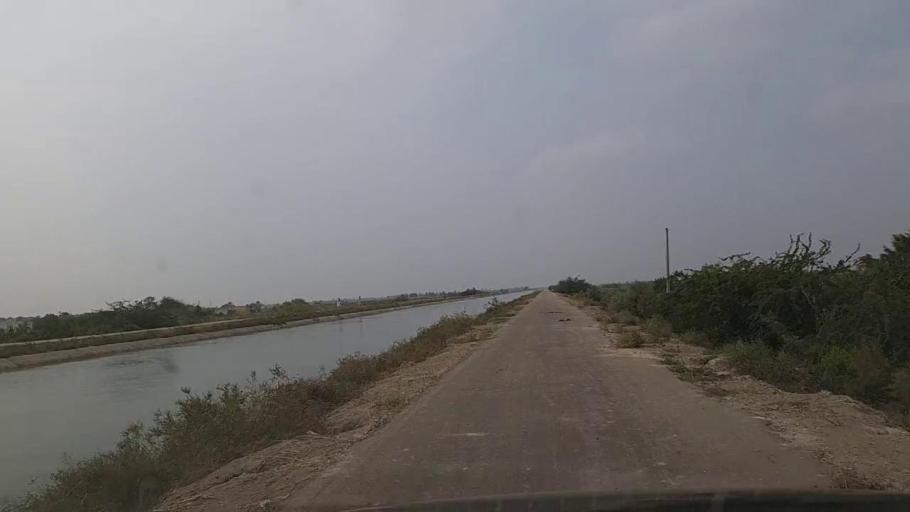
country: PK
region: Sindh
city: Thatta
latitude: 24.8035
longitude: 67.8983
